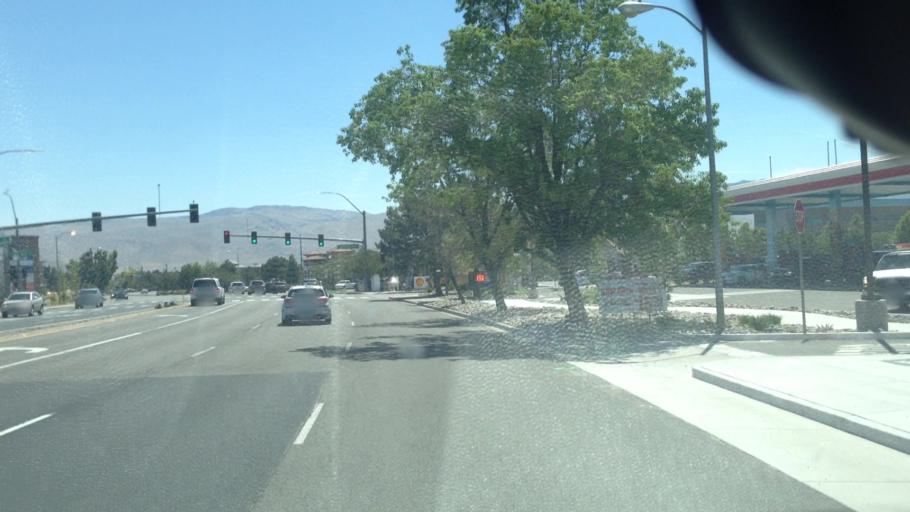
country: US
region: Nevada
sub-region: Washoe County
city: Sparks
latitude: 39.4383
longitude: -119.7626
